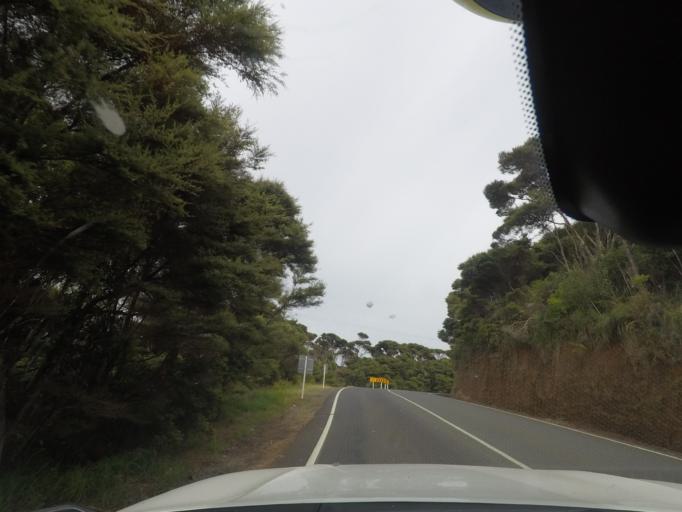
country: NZ
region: Auckland
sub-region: Auckland
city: Parakai
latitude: -36.4903
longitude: 174.2479
